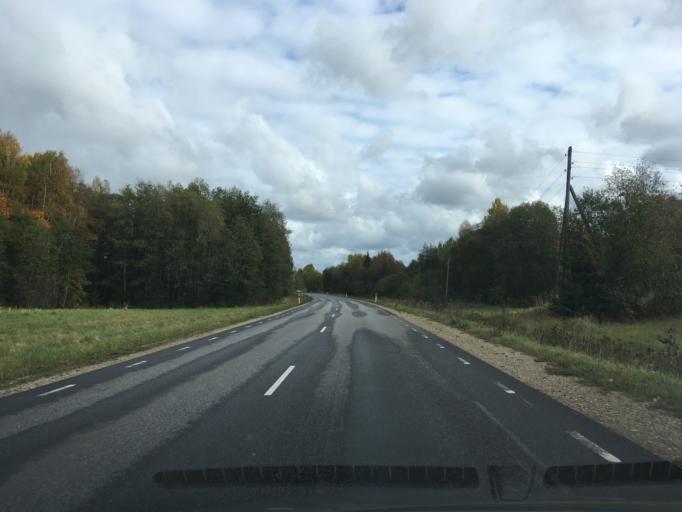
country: EE
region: Harju
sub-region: Anija vald
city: Kehra
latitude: 59.2243
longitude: 25.2691
